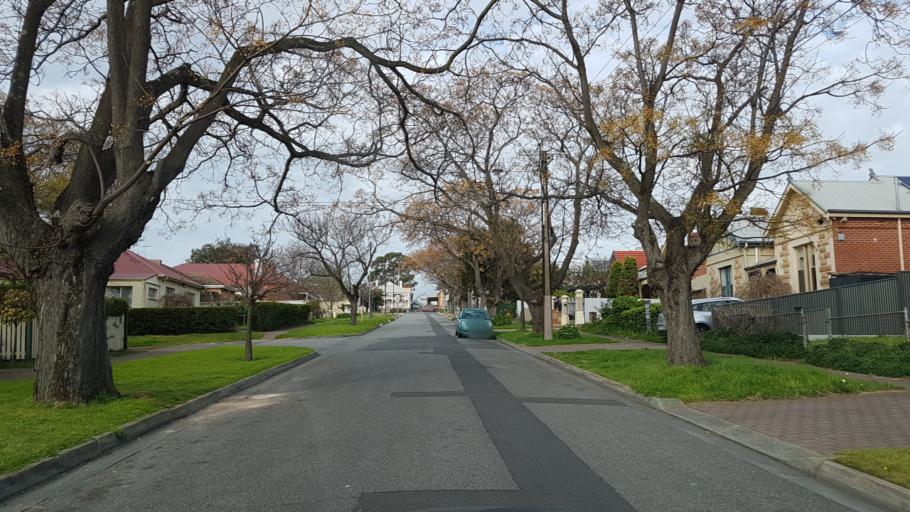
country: AU
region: South Australia
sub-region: Prospect
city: Prospect
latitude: -34.8774
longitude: 138.5915
